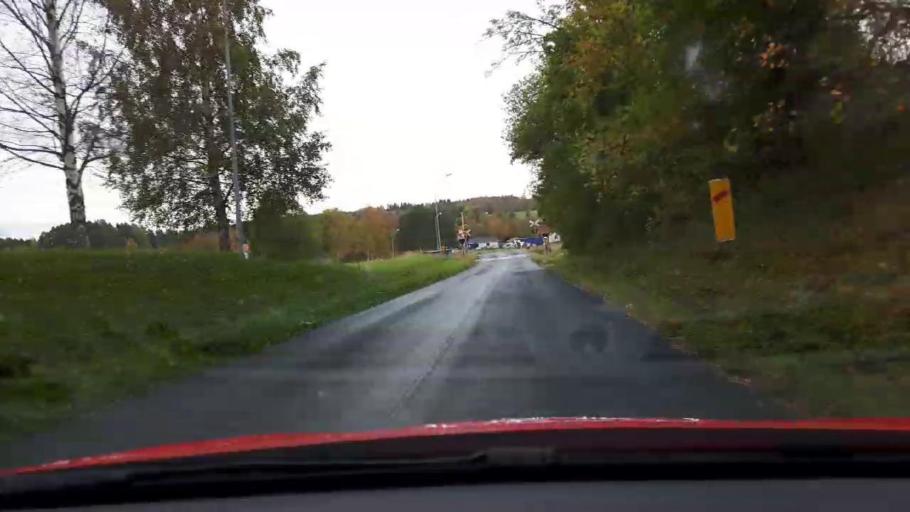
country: SE
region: Jaemtland
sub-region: Bergs Kommun
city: Hoverberg
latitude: 62.9172
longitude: 14.5213
